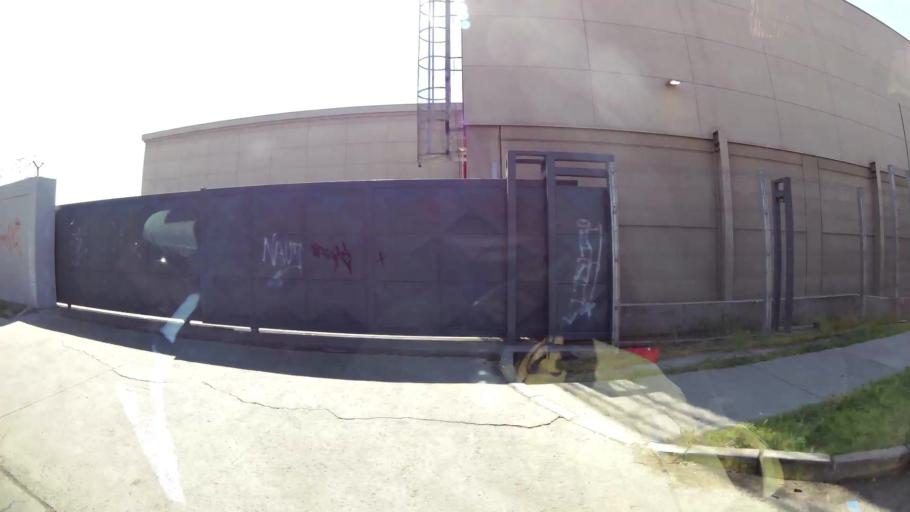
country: CL
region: Santiago Metropolitan
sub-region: Provincia de Santiago
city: Lo Prado
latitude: -33.3588
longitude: -70.7283
